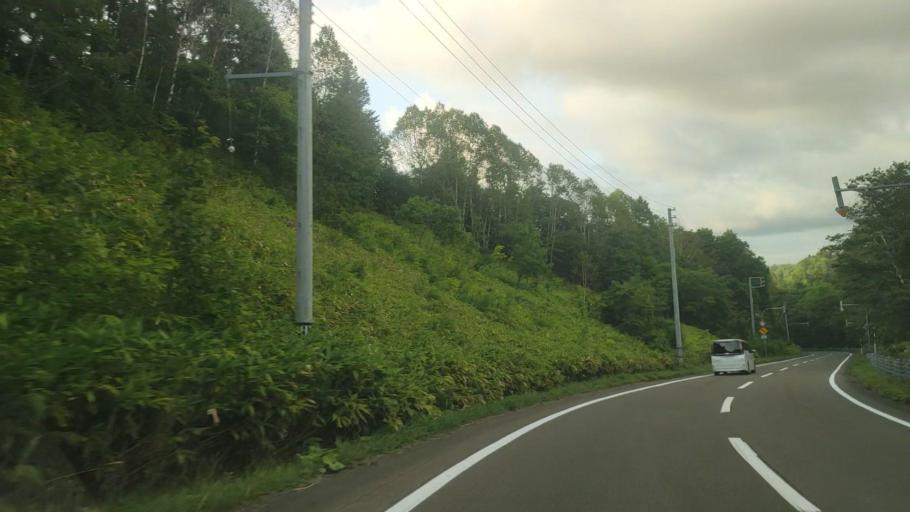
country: JP
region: Hokkaido
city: Bibai
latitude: 43.1694
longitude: 142.0720
